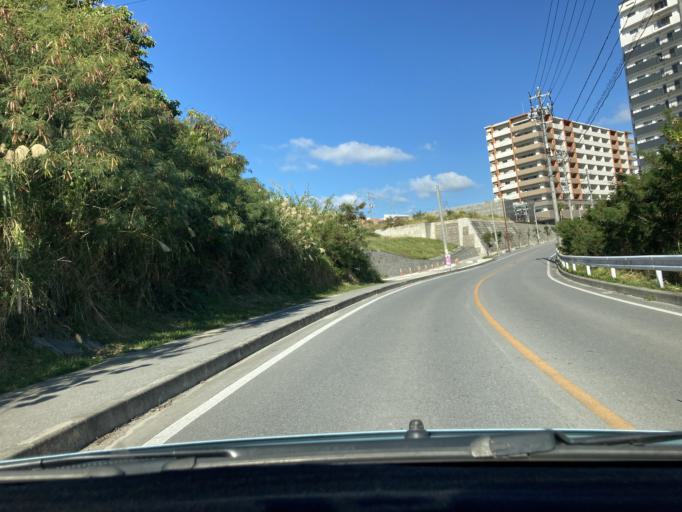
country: JP
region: Okinawa
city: Chatan
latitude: 26.3080
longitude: 127.7963
